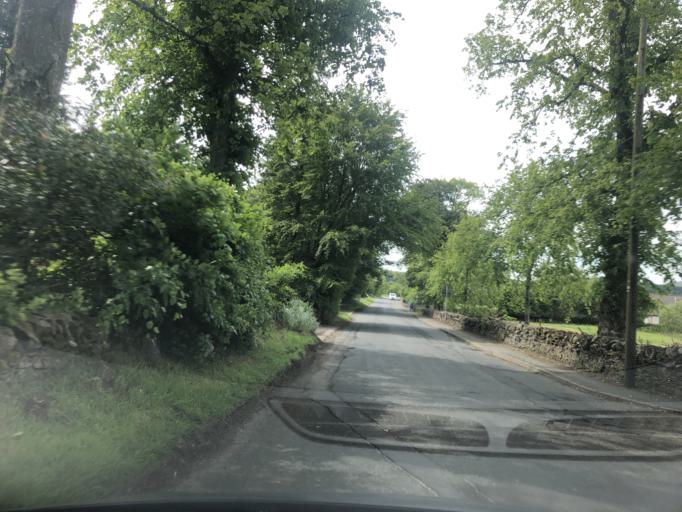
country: GB
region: Scotland
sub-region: The Scottish Borders
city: West Linton
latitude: 55.7439
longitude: -3.3456
